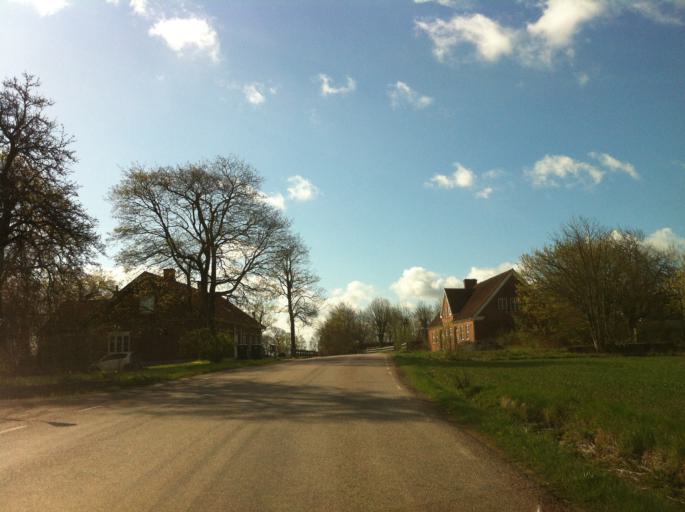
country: SE
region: Skane
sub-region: Eslovs Kommun
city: Stehag
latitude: 55.9178
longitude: 13.3839
